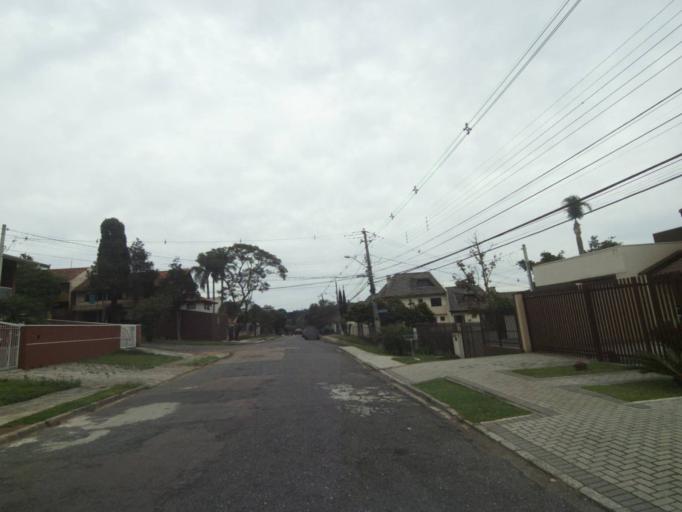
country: BR
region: Parana
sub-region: Curitiba
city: Curitiba
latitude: -25.3976
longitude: -49.2670
